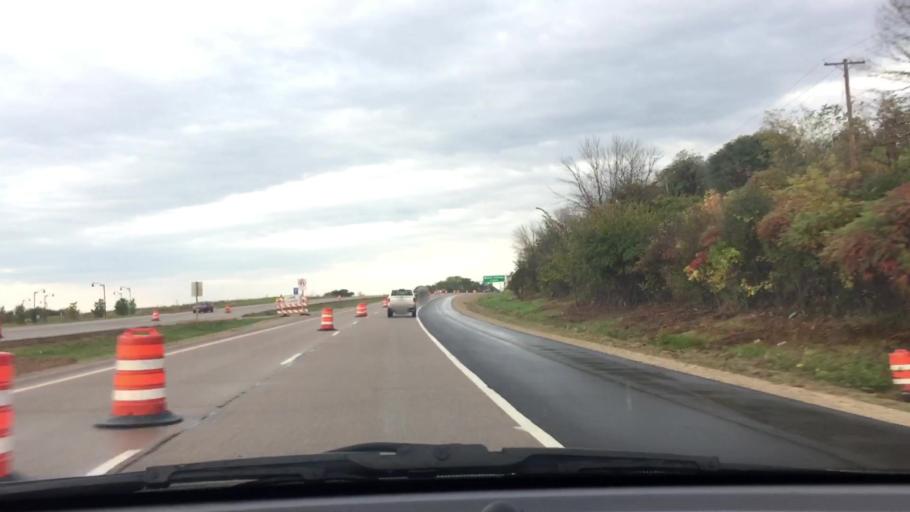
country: US
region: Wisconsin
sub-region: Rock County
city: Beloit
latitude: 42.5342
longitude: -88.9578
